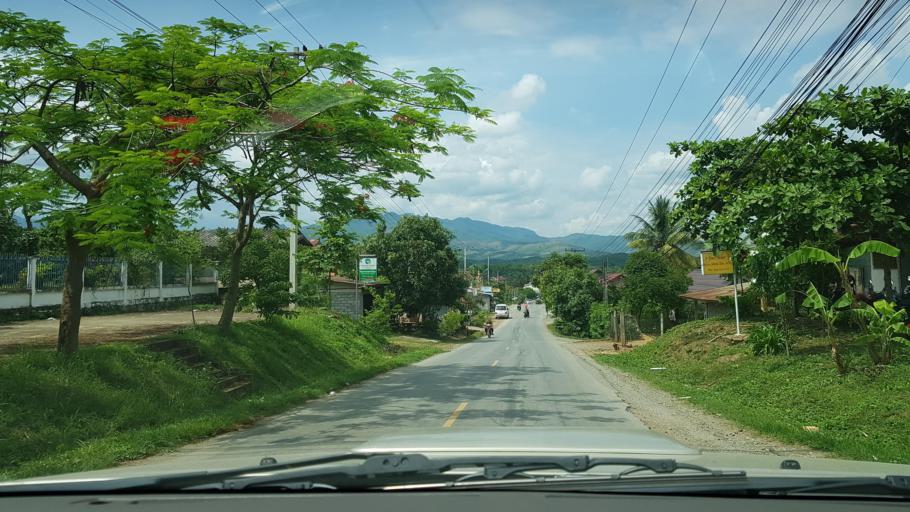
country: LA
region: Loungnamtha
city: Muang Nale
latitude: 20.1417
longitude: 101.4552
